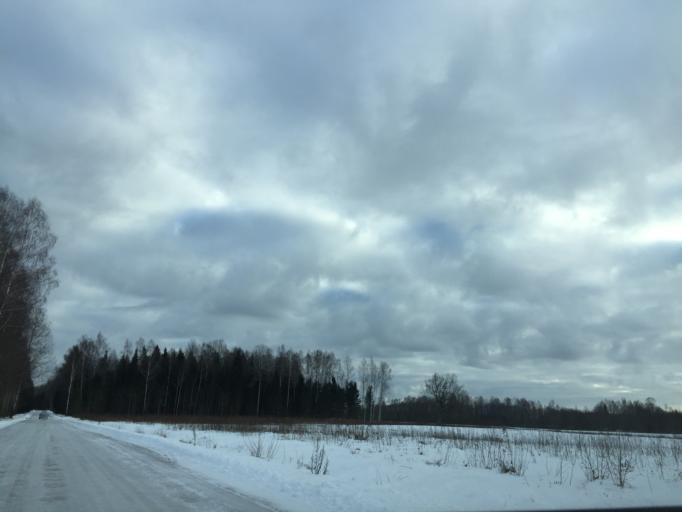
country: LV
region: Lielvarde
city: Lielvarde
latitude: 56.5839
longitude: 24.7407
